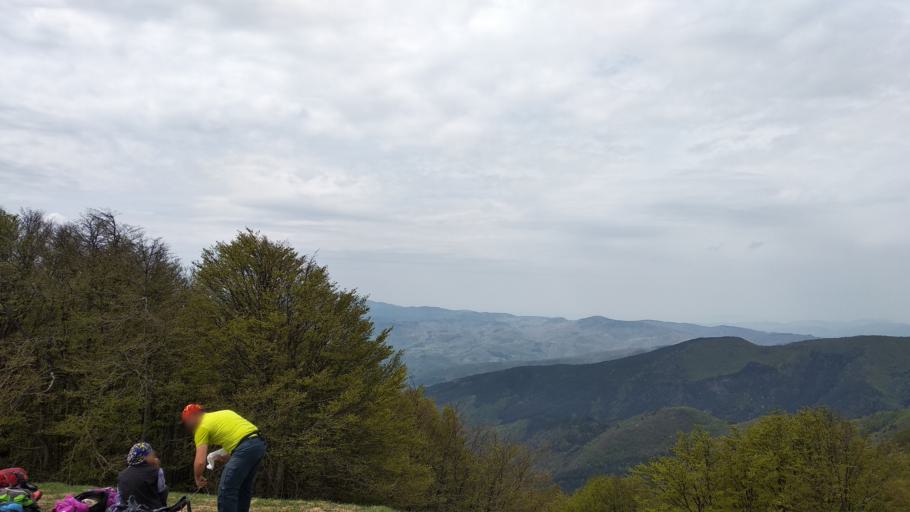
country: IT
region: Tuscany
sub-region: Province of Arezzo
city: Pratovecchio
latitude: 43.8449
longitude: 11.7885
